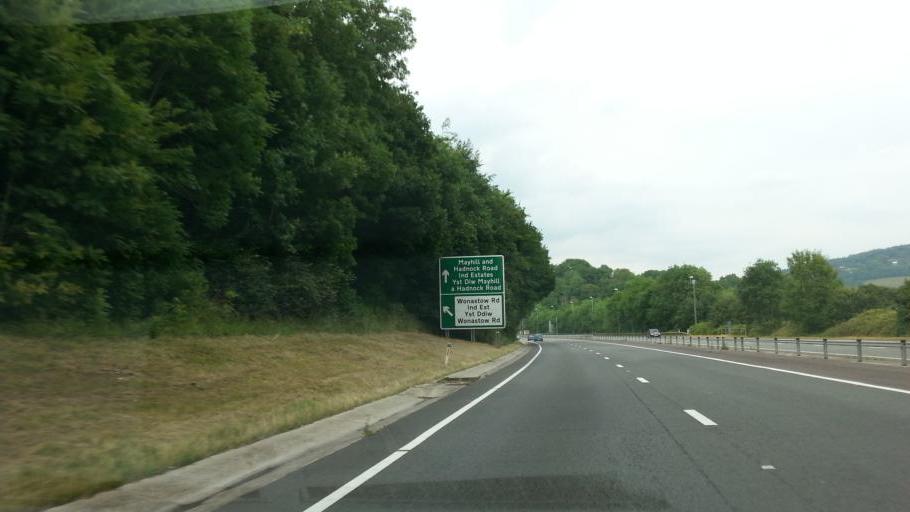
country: GB
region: Wales
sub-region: Monmouthshire
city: Monmouth
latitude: 51.7994
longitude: -2.7222
